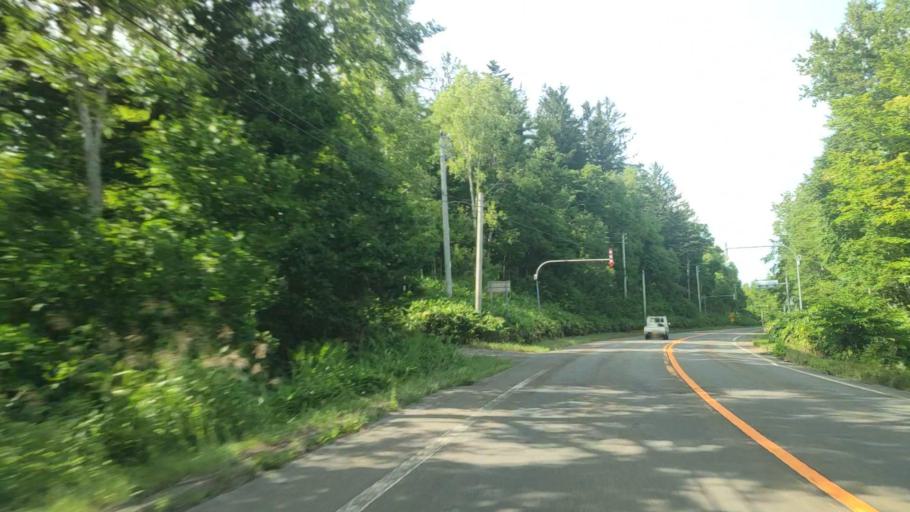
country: JP
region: Hokkaido
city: Nayoro
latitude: 44.3872
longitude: 142.3978
